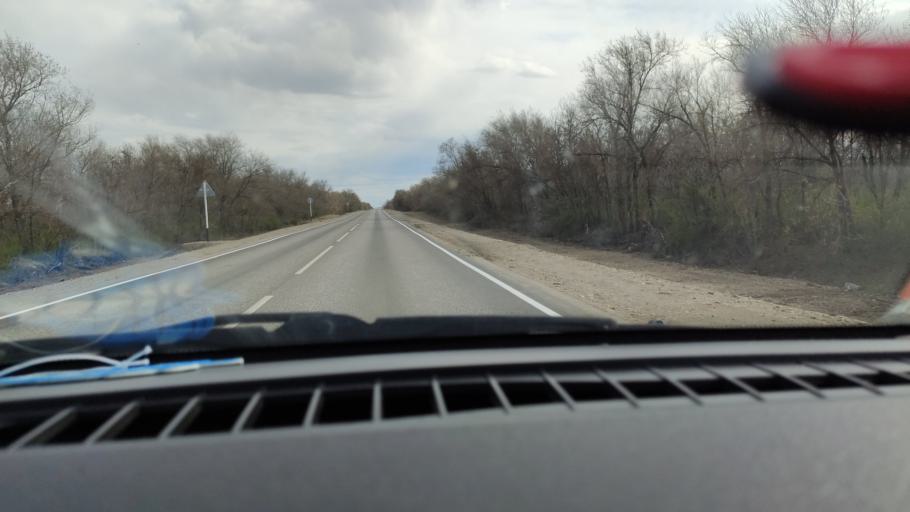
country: RU
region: Saratov
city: Krasnoarmeysk
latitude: 51.0954
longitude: 45.9554
